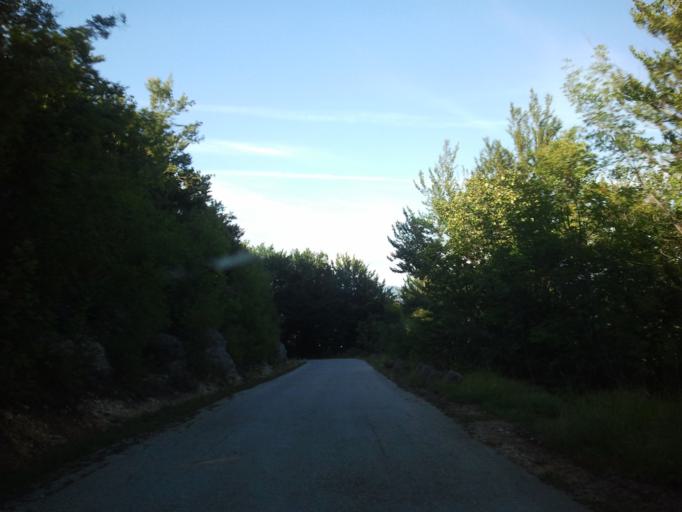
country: HR
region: Zadarska
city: Obrovac
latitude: 44.3269
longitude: 15.6434
